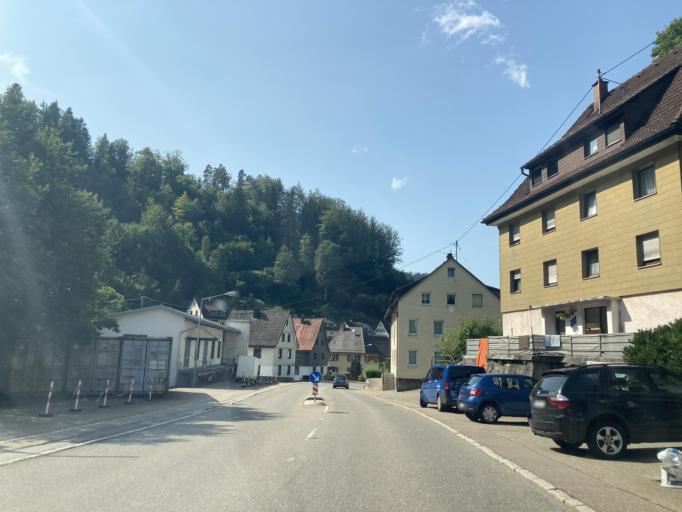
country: DE
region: Baden-Wuerttemberg
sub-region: Freiburg Region
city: Triberg im Schwarzwald
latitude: 48.1341
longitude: 8.2473
